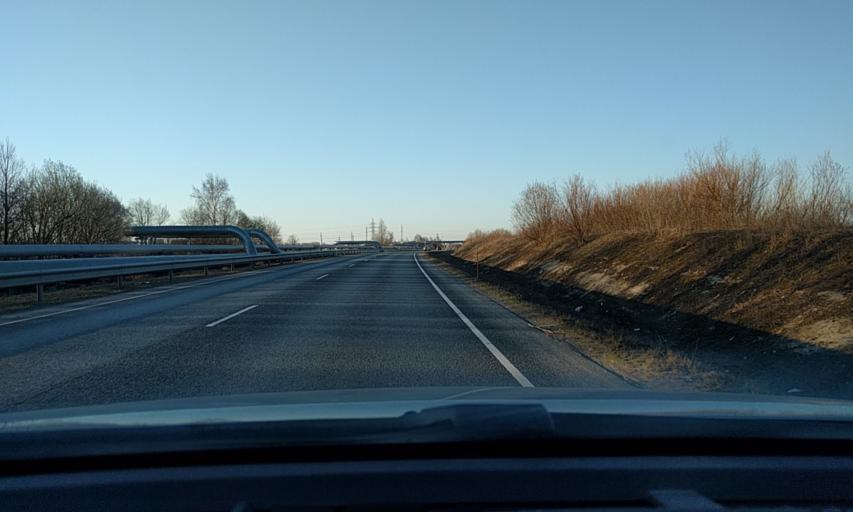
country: EE
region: Harju
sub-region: Maardu linn
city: Maardu
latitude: 59.4738
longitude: 24.9812
